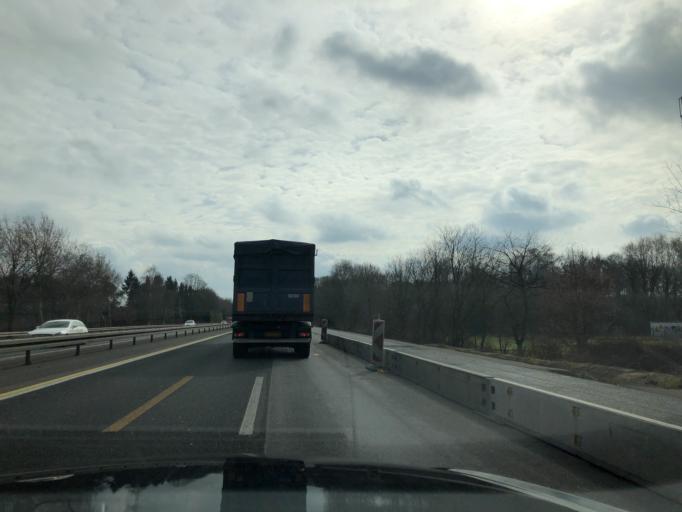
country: DE
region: North Rhine-Westphalia
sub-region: Regierungsbezirk Dusseldorf
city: Hunxe
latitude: 51.6267
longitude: 6.7549
